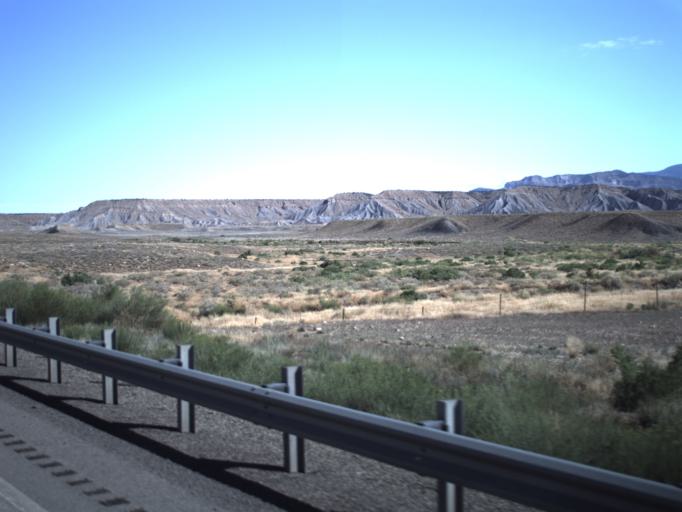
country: US
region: Utah
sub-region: Carbon County
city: East Carbon City
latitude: 39.3795
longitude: -110.4050
